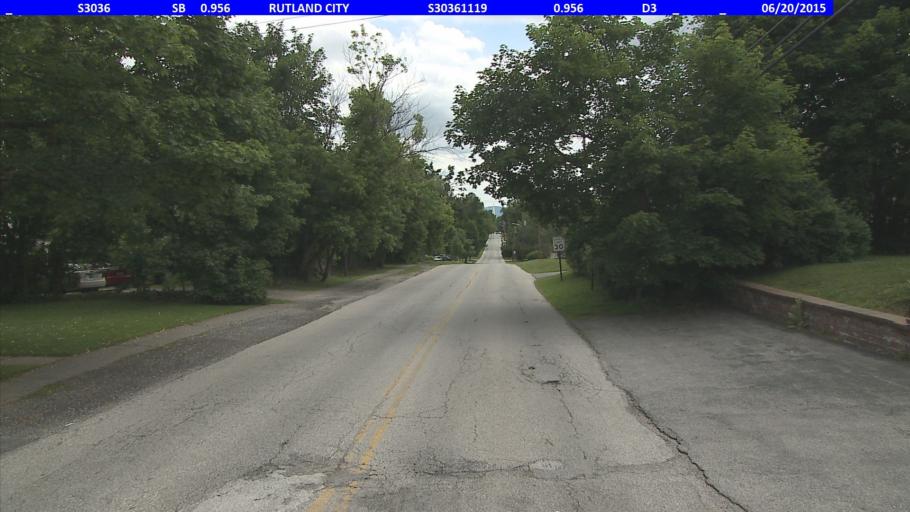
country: US
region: Vermont
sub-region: Rutland County
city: Rutland
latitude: 43.6220
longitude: -72.9782
